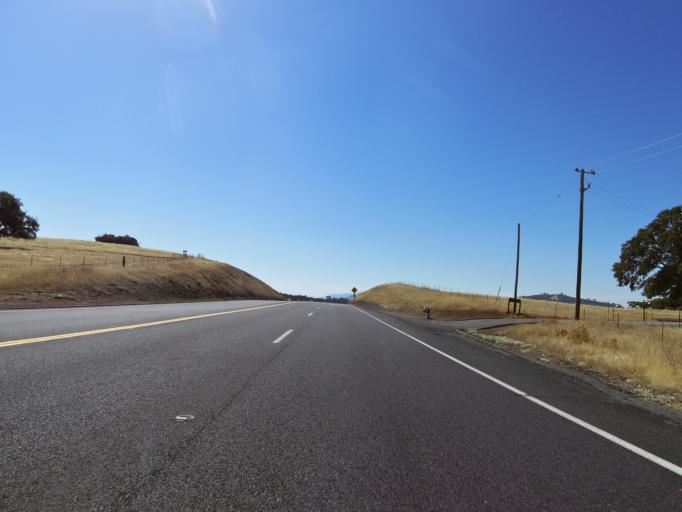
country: US
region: California
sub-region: Tuolumne County
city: Tuolumne City
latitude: 37.7096
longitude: -120.3120
